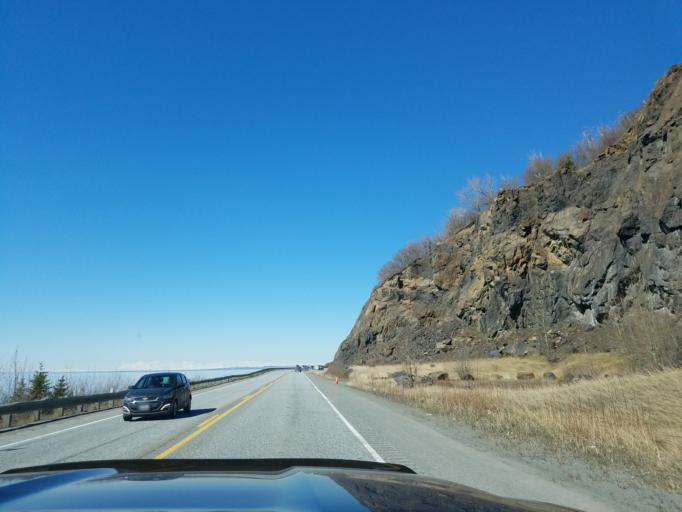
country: US
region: Alaska
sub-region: Anchorage Municipality
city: Anchorage
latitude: 61.0305
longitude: -149.7626
